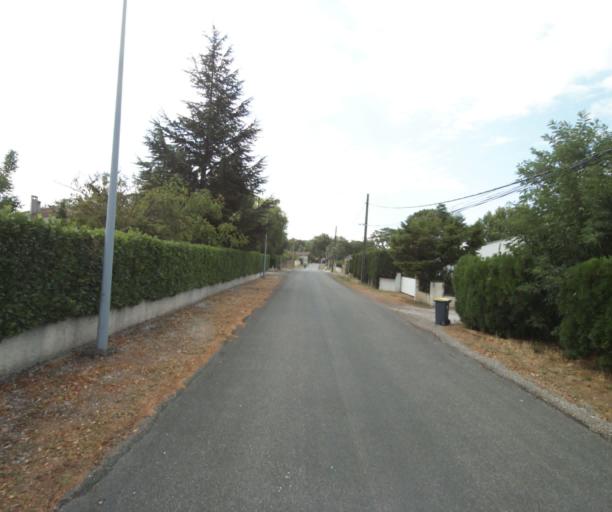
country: FR
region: Midi-Pyrenees
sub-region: Departement de la Haute-Garonne
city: Revel
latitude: 43.4653
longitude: 1.9985
